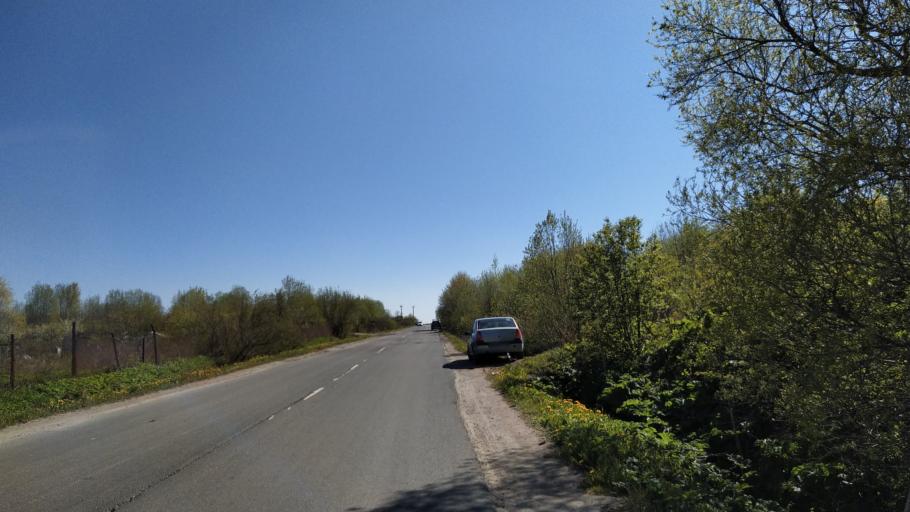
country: RU
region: St.-Petersburg
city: Pushkin
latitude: 59.6893
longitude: 30.3956
